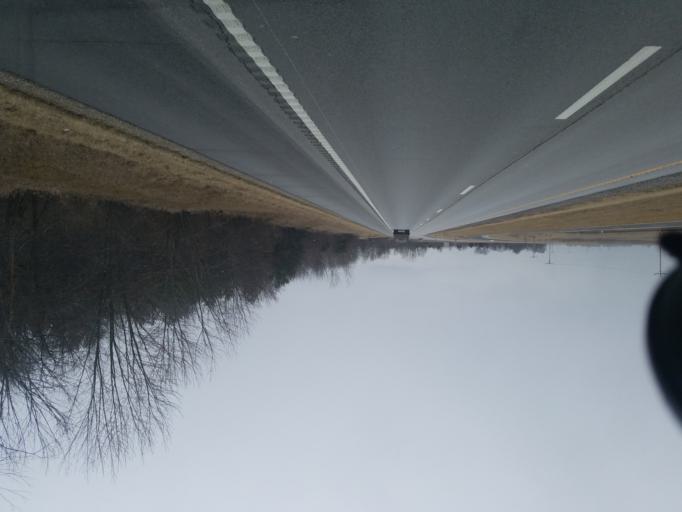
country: US
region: Missouri
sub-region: Macon County
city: Macon
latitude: 39.8700
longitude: -92.4784
